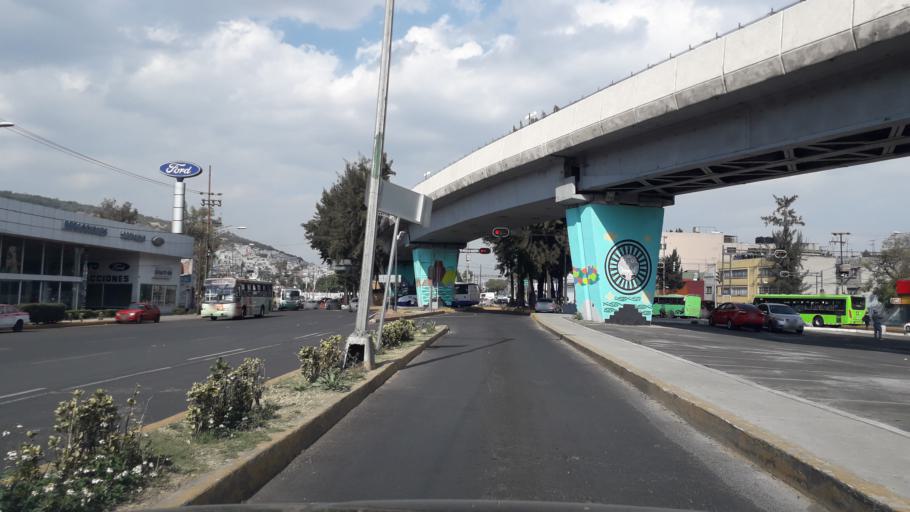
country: MX
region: Mexico City
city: Gustavo A. Madero
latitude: 19.4810
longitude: -99.1070
